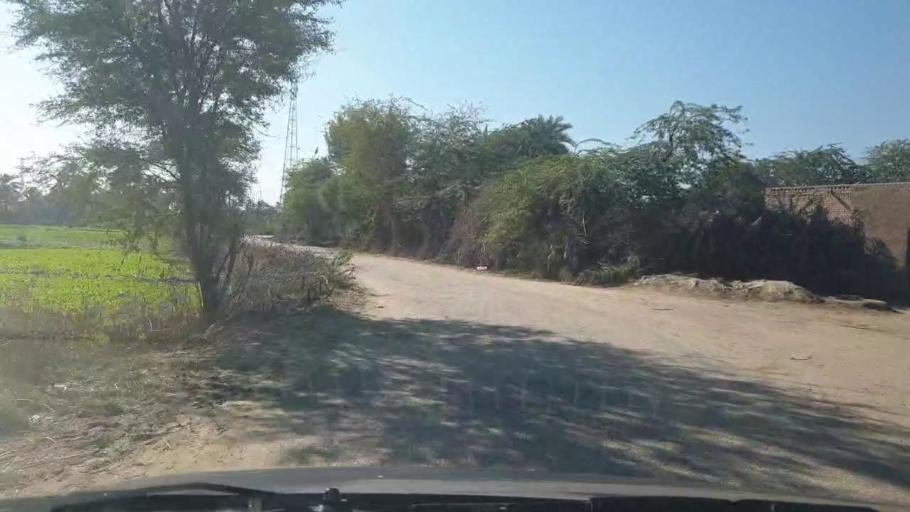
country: PK
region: Sindh
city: Bozdar
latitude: 27.1464
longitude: 68.6482
